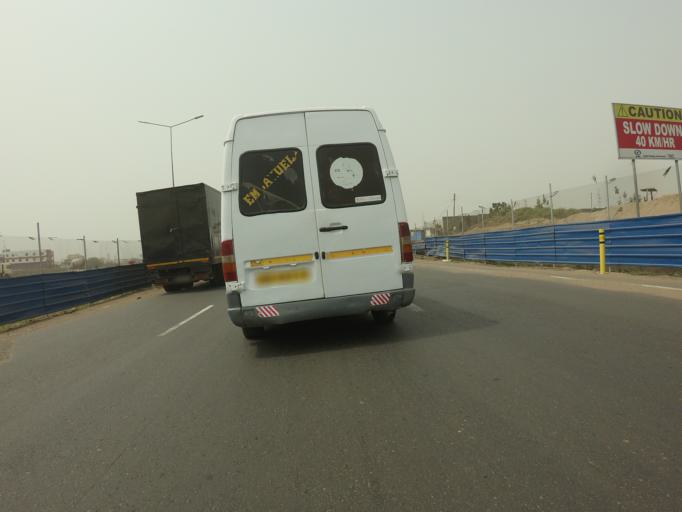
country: GH
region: Greater Accra
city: Tema
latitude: 5.6861
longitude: -0.0163
